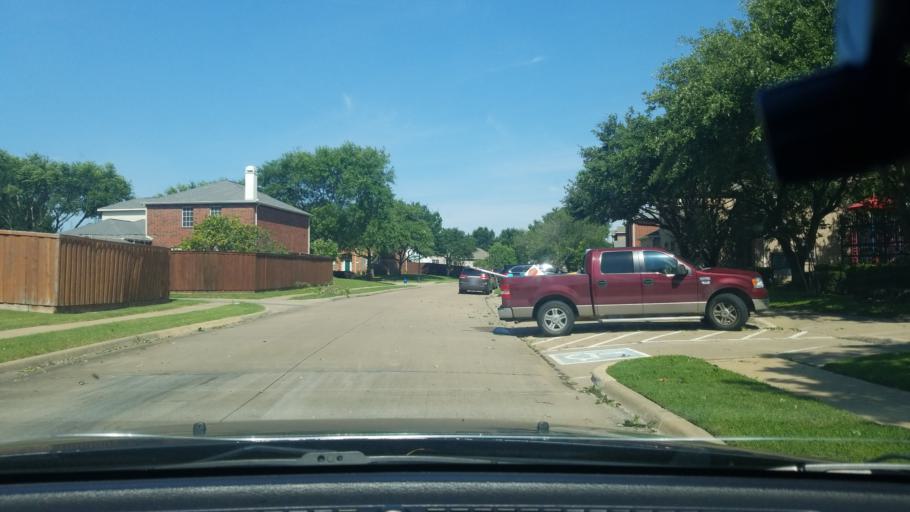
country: US
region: Texas
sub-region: Dallas County
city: Mesquite
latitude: 32.7715
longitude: -96.5864
